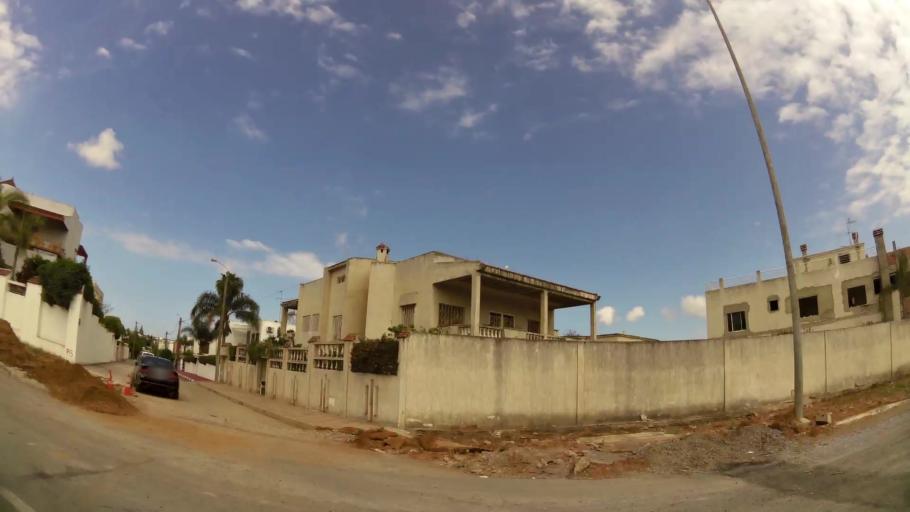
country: MA
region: Gharb-Chrarda-Beni Hssen
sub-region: Kenitra Province
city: Kenitra
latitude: 34.2466
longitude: -6.5956
